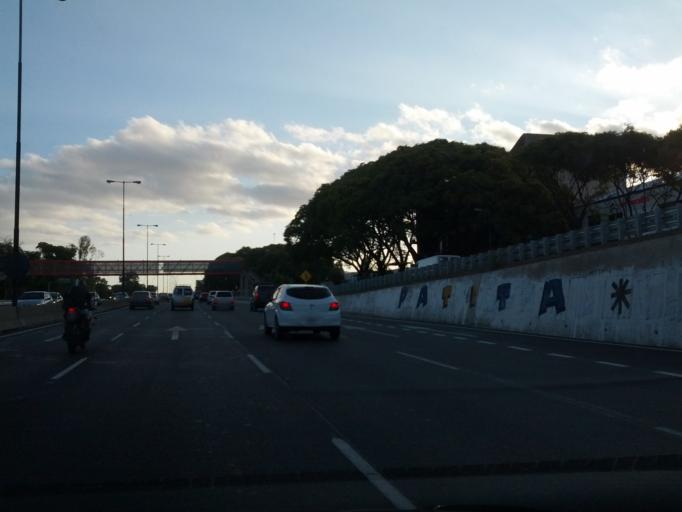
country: AR
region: Buenos Aires
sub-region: Partido de General San Martin
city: General San Martin
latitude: -34.5908
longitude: -58.5194
